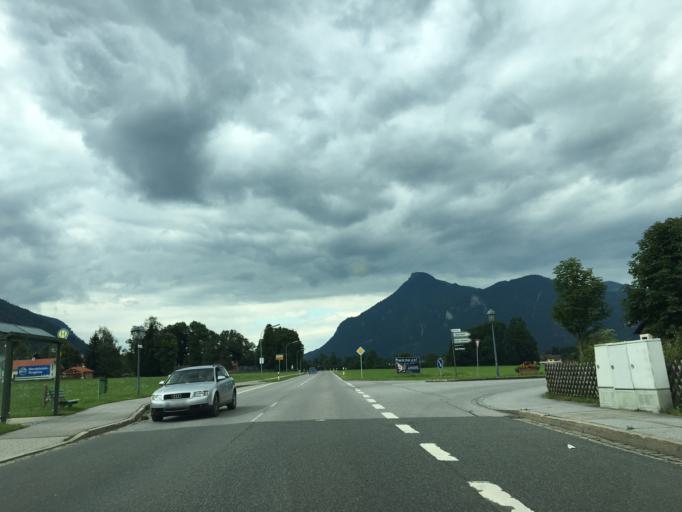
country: DE
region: Bavaria
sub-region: Upper Bavaria
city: Oberaudorf
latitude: 47.6524
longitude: 12.1729
